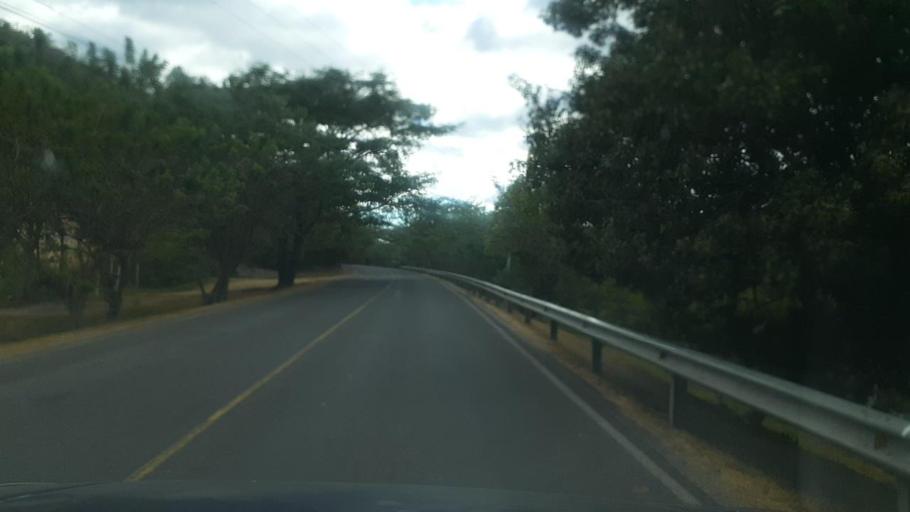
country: NI
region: Madriz
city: Somoto
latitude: 13.4981
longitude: -86.5734
